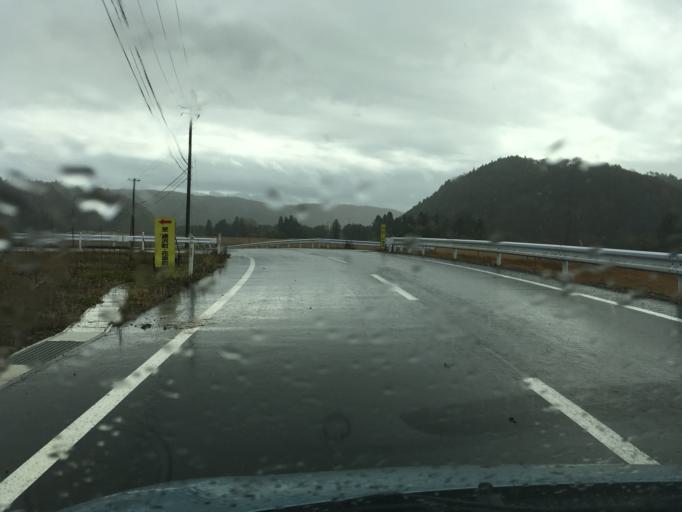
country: JP
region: Iwate
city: Ichinoseki
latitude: 38.7940
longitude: 141.2497
